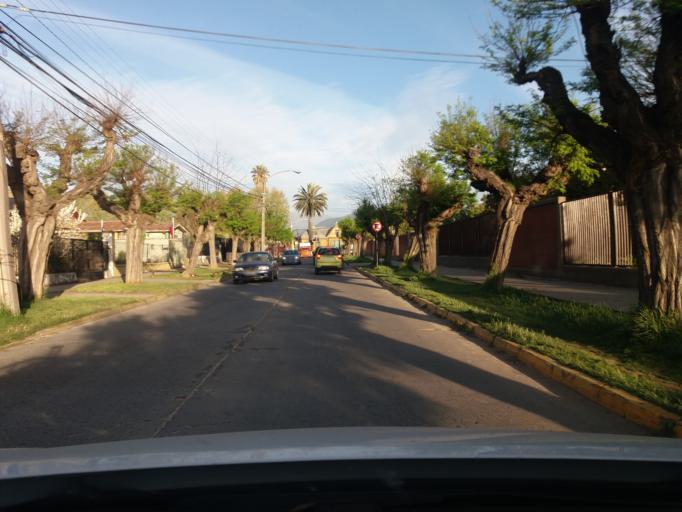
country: CL
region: Valparaiso
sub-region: Provincia de Marga Marga
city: Limache
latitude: -32.9925
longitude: -71.2663
